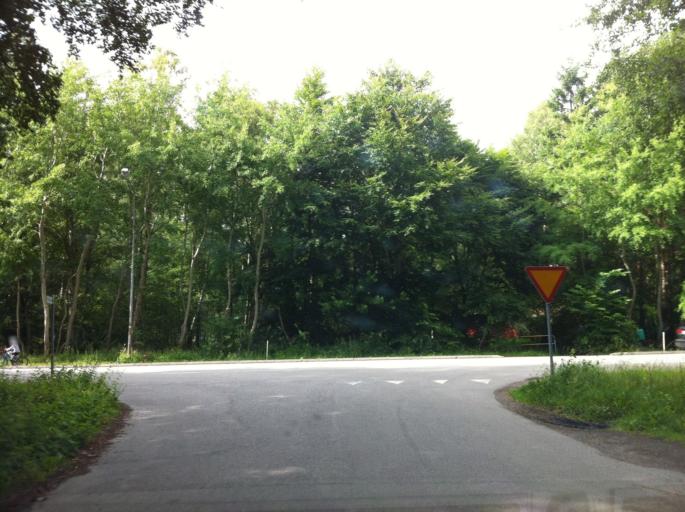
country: SE
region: Skane
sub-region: Ystads Kommun
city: Ystad
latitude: 55.4310
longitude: 13.8610
